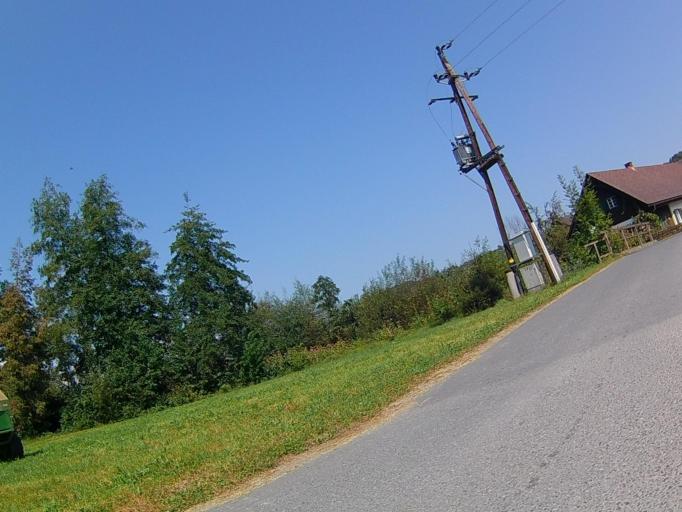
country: AT
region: Styria
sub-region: Politischer Bezirk Leibnitz
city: Oberhaag
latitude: 46.6898
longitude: 15.3227
